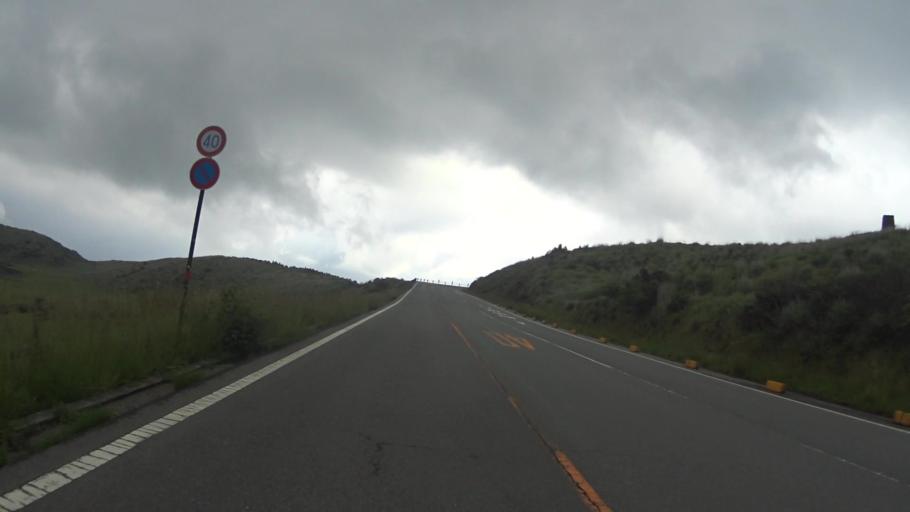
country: JP
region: Kumamoto
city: Aso
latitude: 32.8846
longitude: 131.0511
